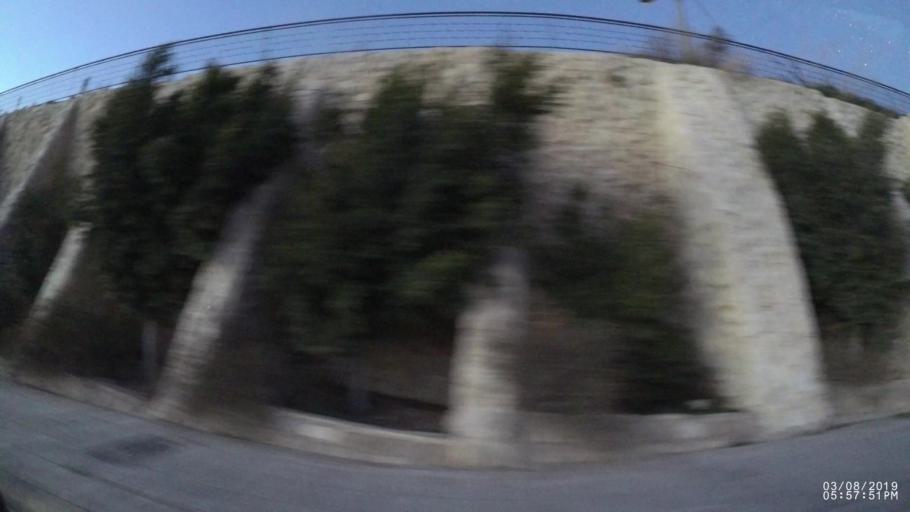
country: JO
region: Ma'an
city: Petra
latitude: 30.3237
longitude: 35.4764
